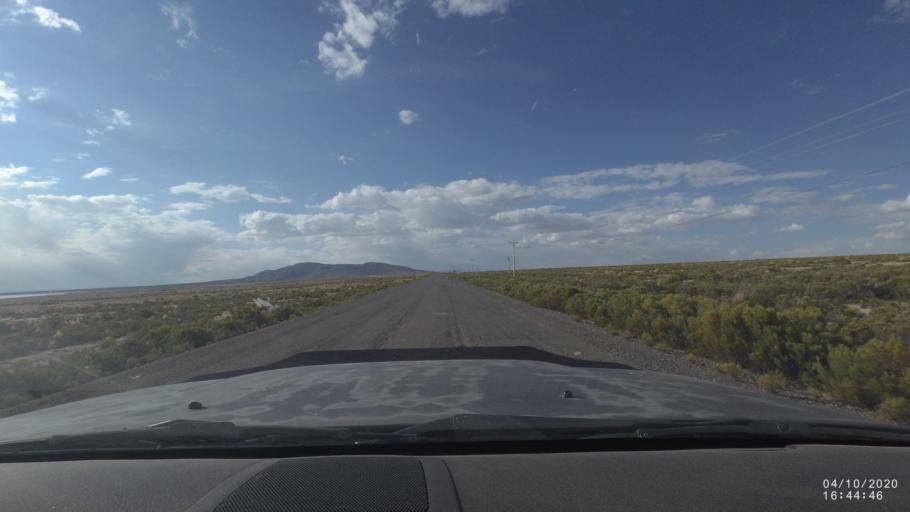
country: BO
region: Oruro
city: Poopo
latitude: -18.6790
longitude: -67.5604
